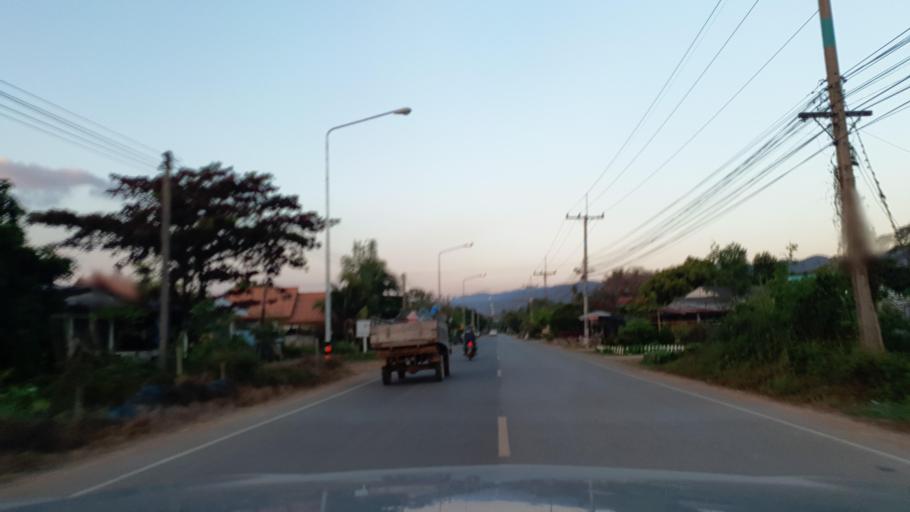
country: TH
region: Phayao
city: Dok Kham Tai
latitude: 19.0302
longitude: 100.0640
